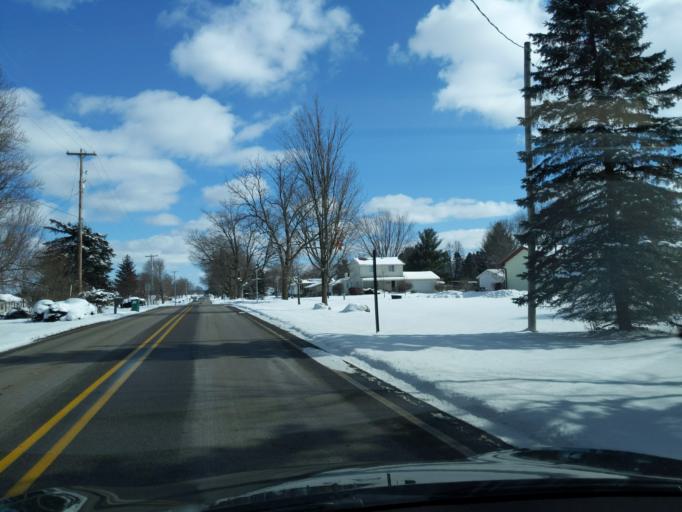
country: US
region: Michigan
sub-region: Eaton County
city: Dimondale
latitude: 42.6474
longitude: -84.6411
